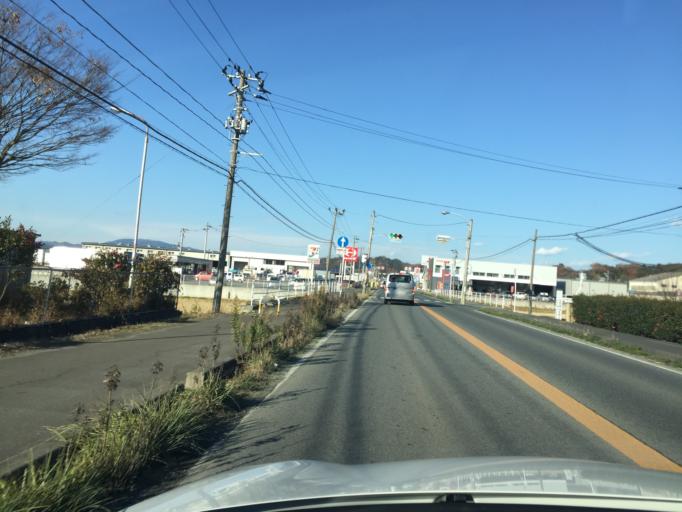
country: JP
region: Fukushima
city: Iwaki
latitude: 36.9751
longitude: 140.8700
